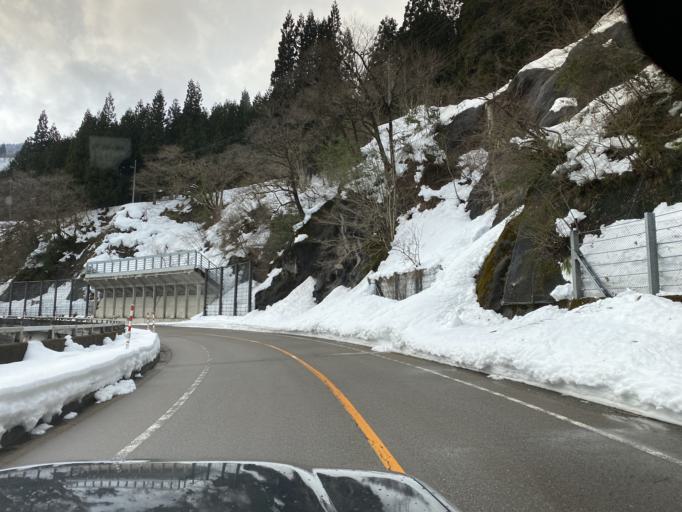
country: JP
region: Toyama
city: Fukumitsu
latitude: 36.3761
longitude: 136.8692
